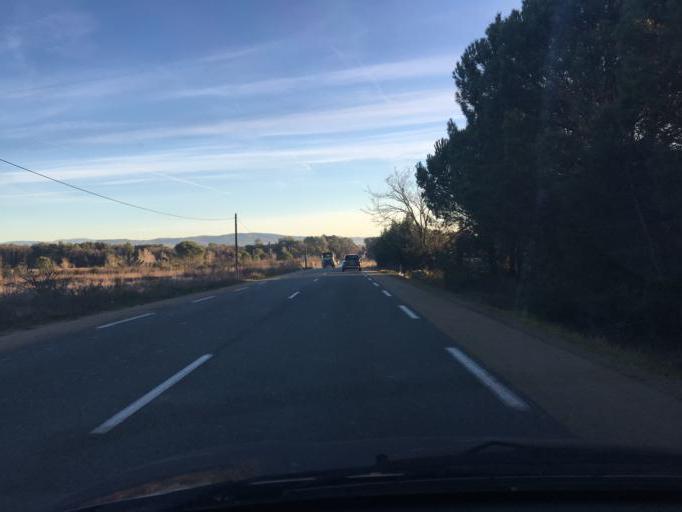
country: FR
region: Provence-Alpes-Cote d'Azur
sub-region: Departement du Var
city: Les Arcs
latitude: 43.4573
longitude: 6.5180
